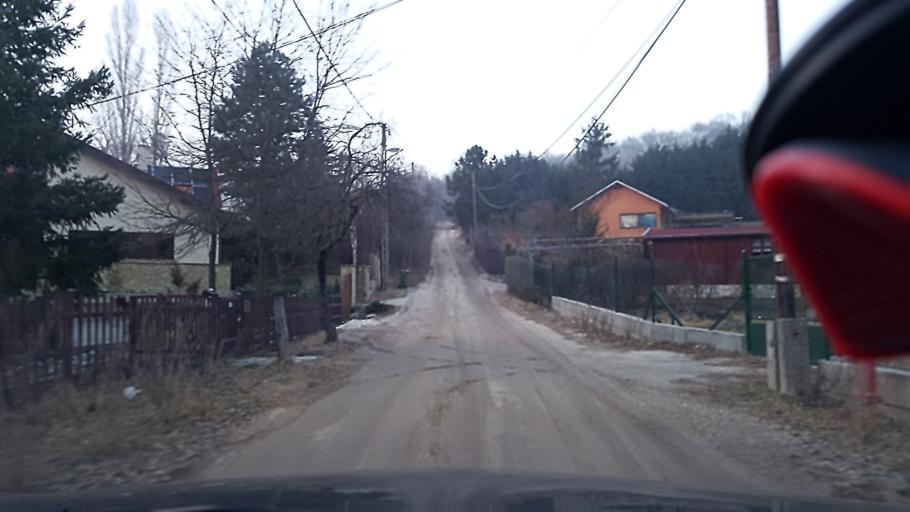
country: HU
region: Pest
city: Piliscsaba
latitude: 47.6447
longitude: 18.8256
